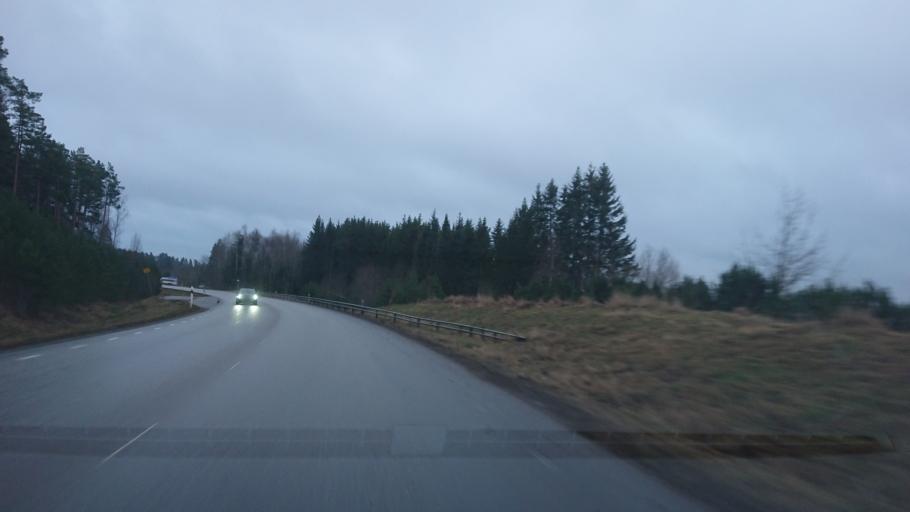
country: SE
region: Uppsala
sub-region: Osthammars Kommun
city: Bjorklinge
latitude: 60.0125
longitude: 17.5878
